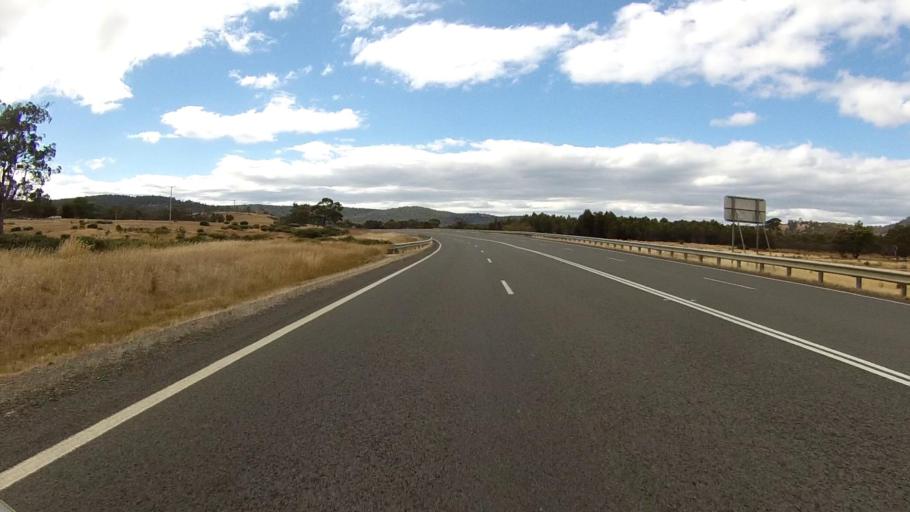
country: AU
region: Tasmania
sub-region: Sorell
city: Sorell
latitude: -42.6433
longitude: 147.5750
